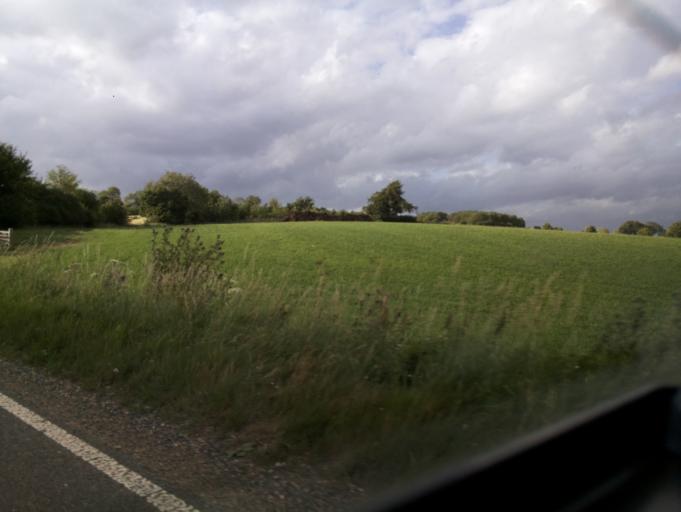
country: GB
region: England
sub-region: Gloucestershire
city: Donnington
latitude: 51.9443
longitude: -1.7309
